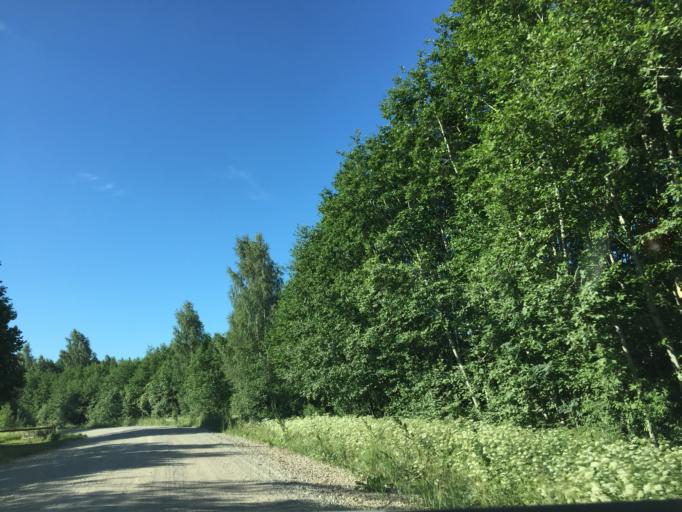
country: LV
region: Ventspils Rajons
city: Piltene
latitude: 57.3176
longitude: 21.6900
